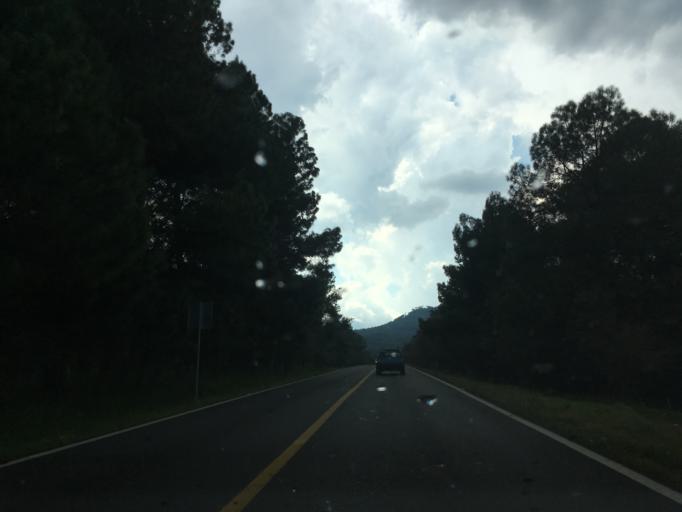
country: MX
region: Michoacan
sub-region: Patzcuaro
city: Santa Maria Huiramangaro (San Juan Tumbio)
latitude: 19.4962
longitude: -101.7743
